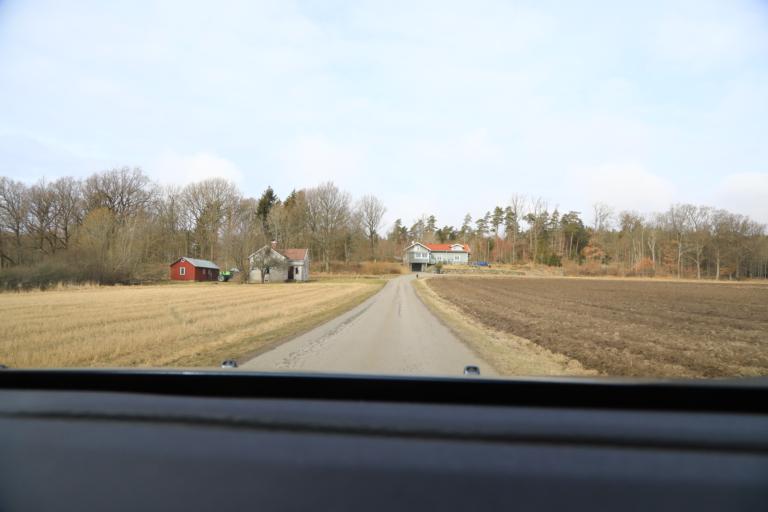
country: SE
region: Halland
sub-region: Varbergs Kommun
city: Veddige
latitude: 57.2106
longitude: 12.2452
